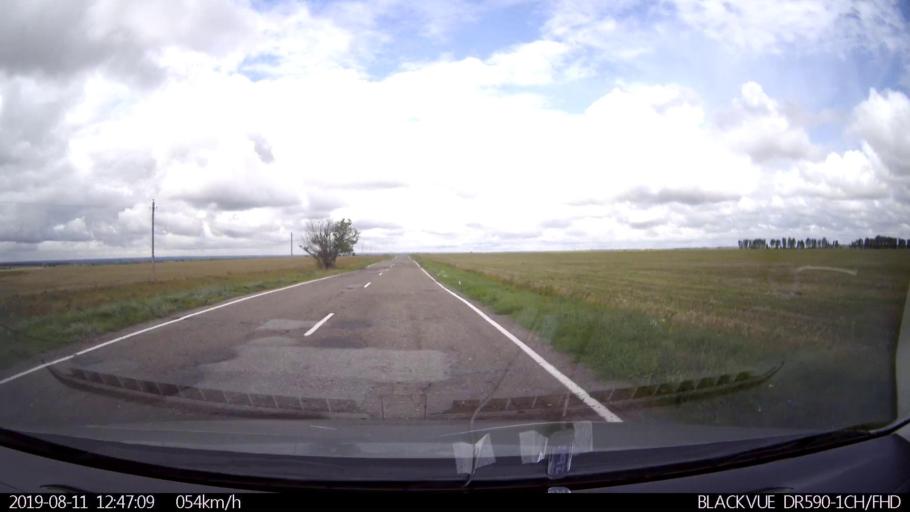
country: RU
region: Ulyanovsk
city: Ignatovka
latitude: 53.8681
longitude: 47.7114
